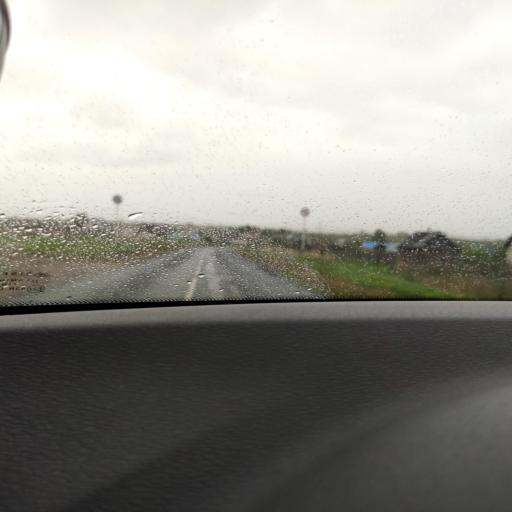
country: RU
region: Samara
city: Yelkhovka
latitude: 53.7449
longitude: 50.2569
